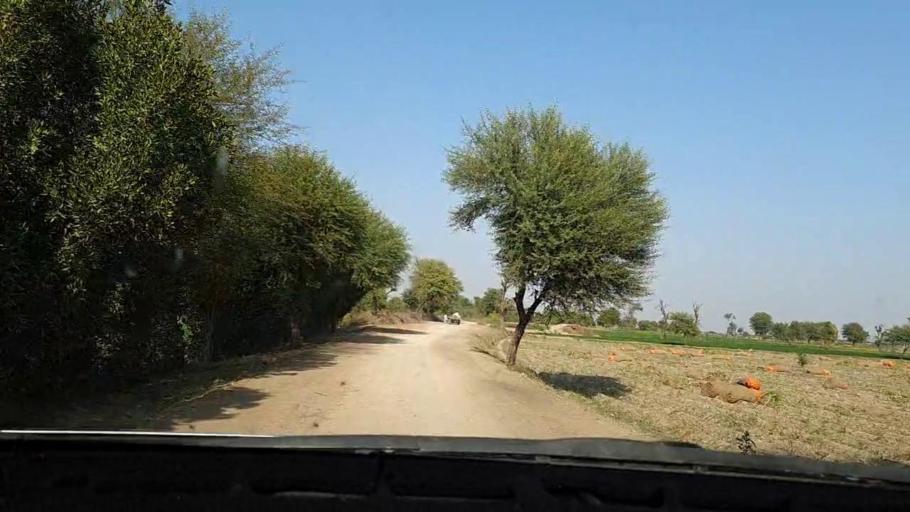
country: PK
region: Sindh
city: Tando Mittha Khan
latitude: 25.8083
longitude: 69.3271
